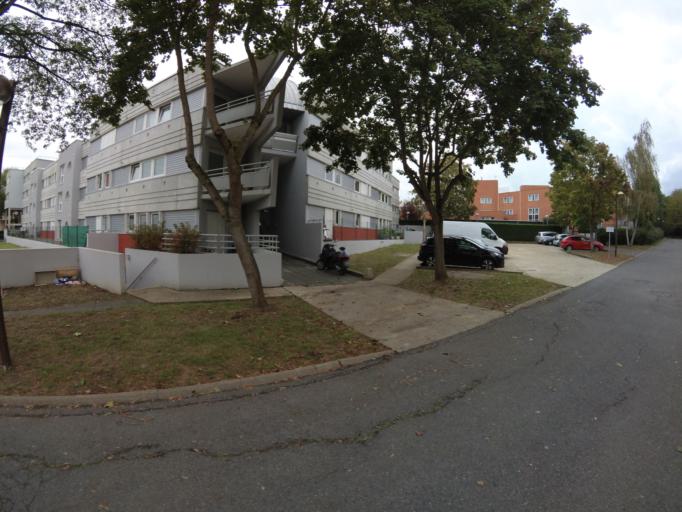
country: FR
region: Ile-de-France
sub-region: Departement de Seine-et-Marne
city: Torcy
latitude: 48.8559
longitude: 2.6666
